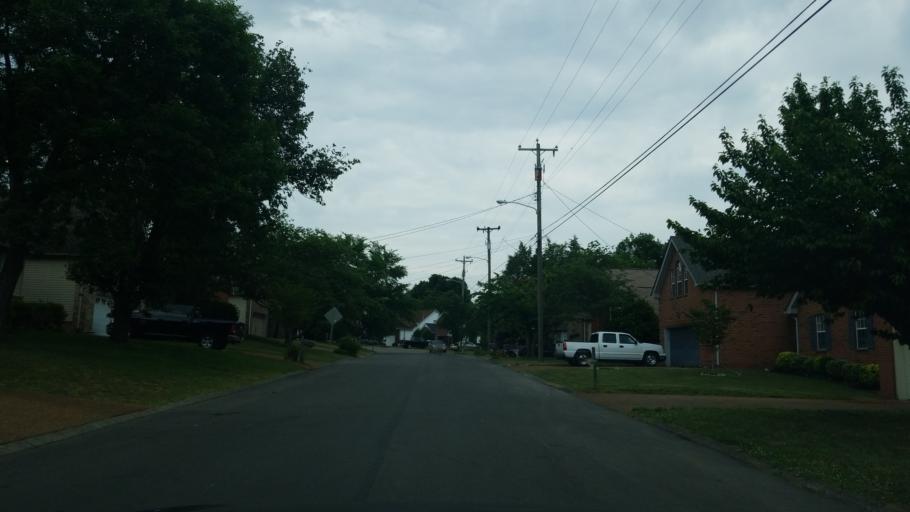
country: US
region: Tennessee
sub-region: Rutherford County
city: La Vergne
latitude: 36.0830
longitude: -86.5859
